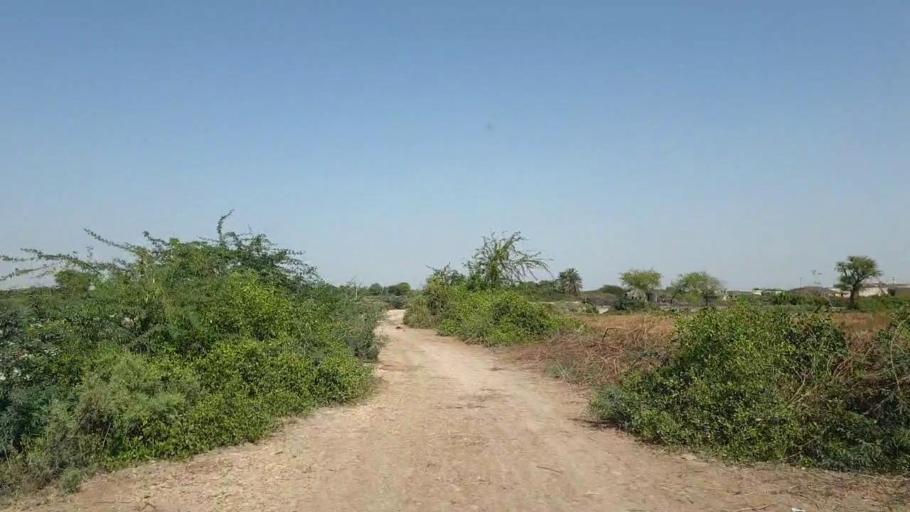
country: PK
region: Sindh
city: Tando Bago
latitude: 24.7234
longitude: 69.0256
